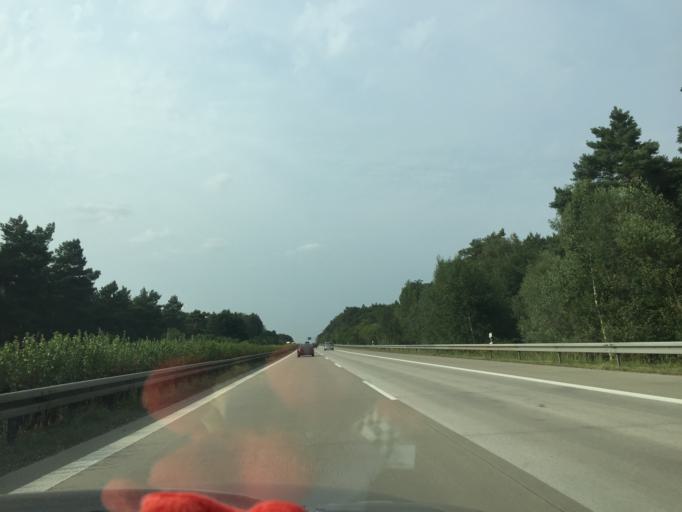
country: DE
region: Brandenburg
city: Bestensee
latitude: 52.2319
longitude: 13.5938
